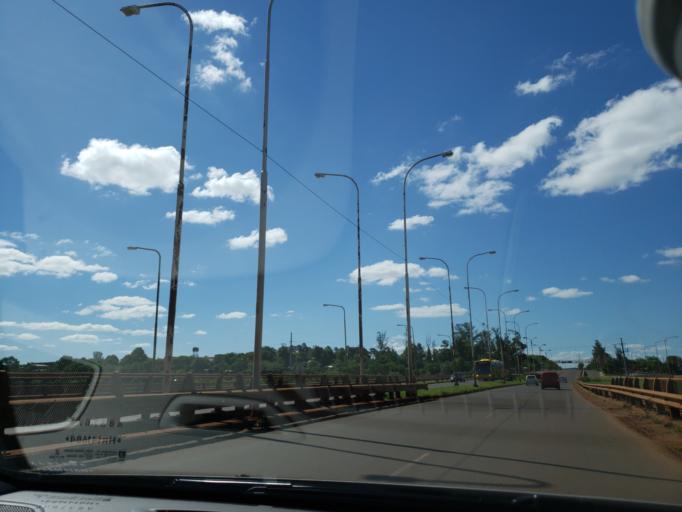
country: AR
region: Misiones
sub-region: Departamento de Capital
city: Posadas
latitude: -27.4202
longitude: -55.8996
